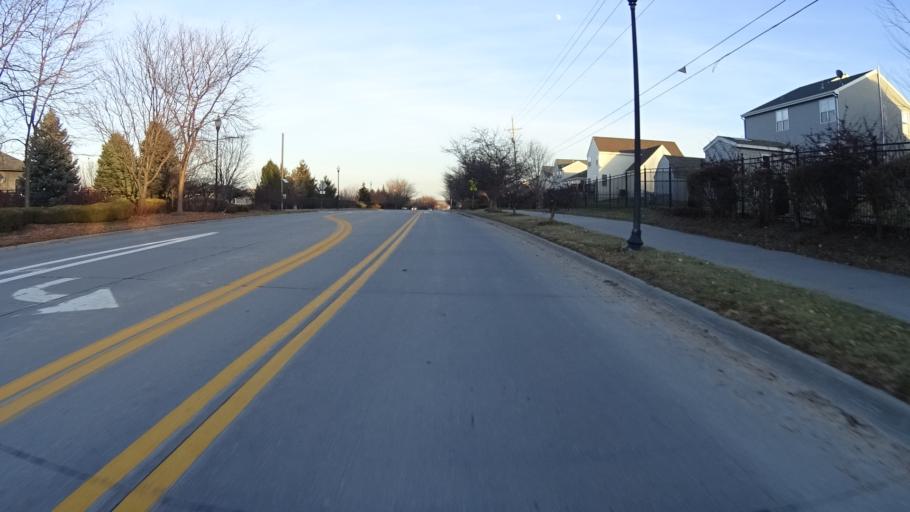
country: US
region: Nebraska
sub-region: Sarpy County
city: Papillion
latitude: 41.1326
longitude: -96.0582
